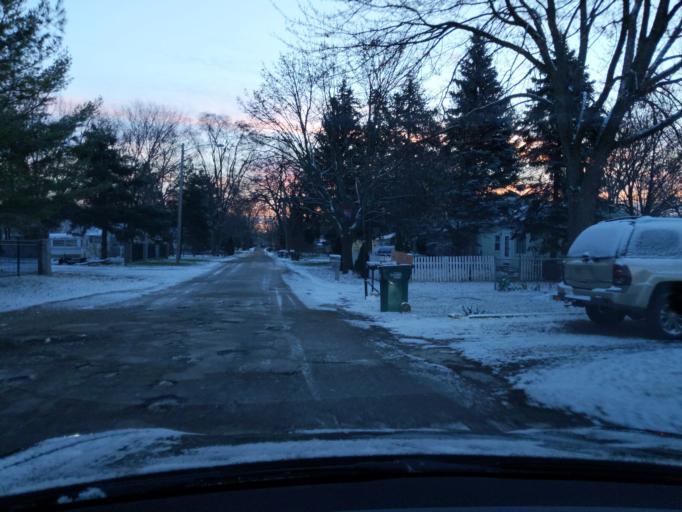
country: US
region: Michigan
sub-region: Ingham County
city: Lansing
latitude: 42.7016
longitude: -84.5669
